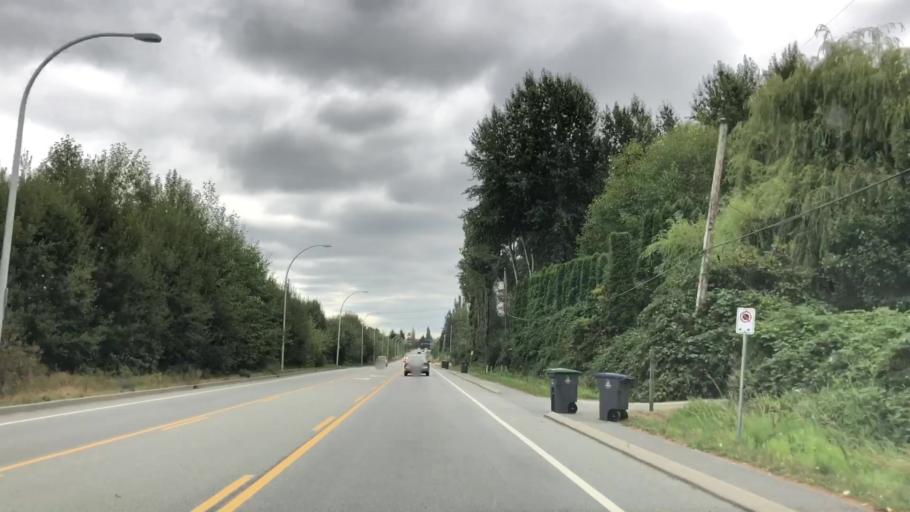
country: CA
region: British Columbia
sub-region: Greater Vancouver Regional District
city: White Rock
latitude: 49.0602
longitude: -122.7657
